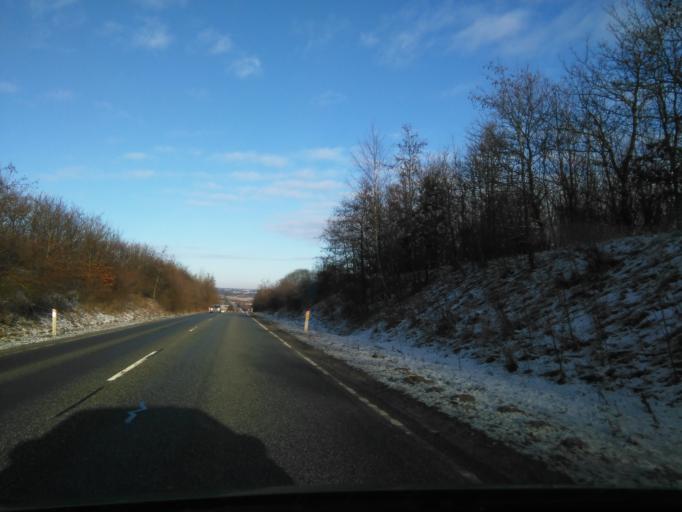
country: DK
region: Central Jutland
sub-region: Arhus Kommune
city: Framlev
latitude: 56.1173
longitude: 9.9873
